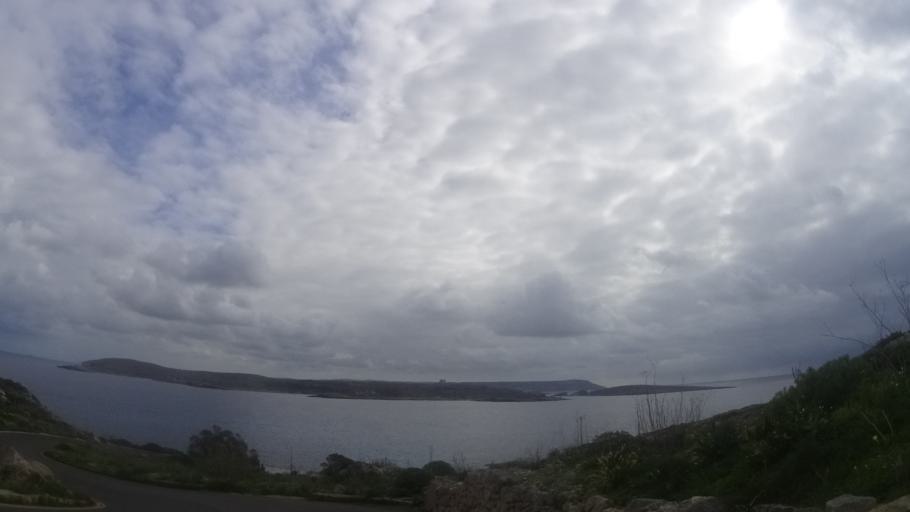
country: MT
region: Il-Qala
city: Qala
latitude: 36.0291
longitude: 14.3222
